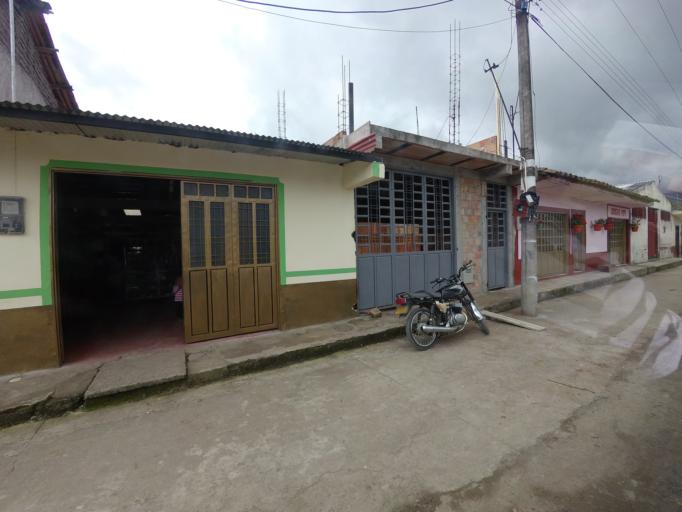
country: CO
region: Huila
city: San Agustin
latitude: 1.9396
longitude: -76.2985
